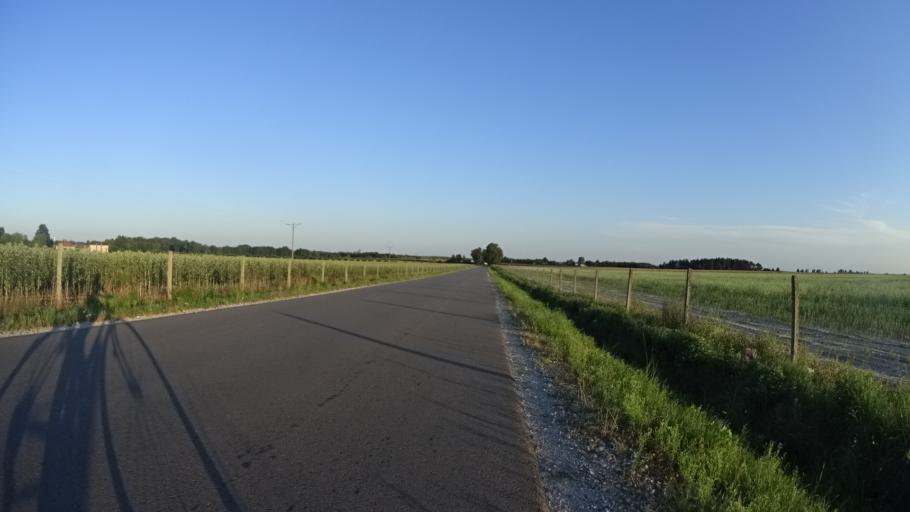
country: PL
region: Masovian Voivodeship
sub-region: Powiat grojecki
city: Goszczyn
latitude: 51.6810
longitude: 20.8259
